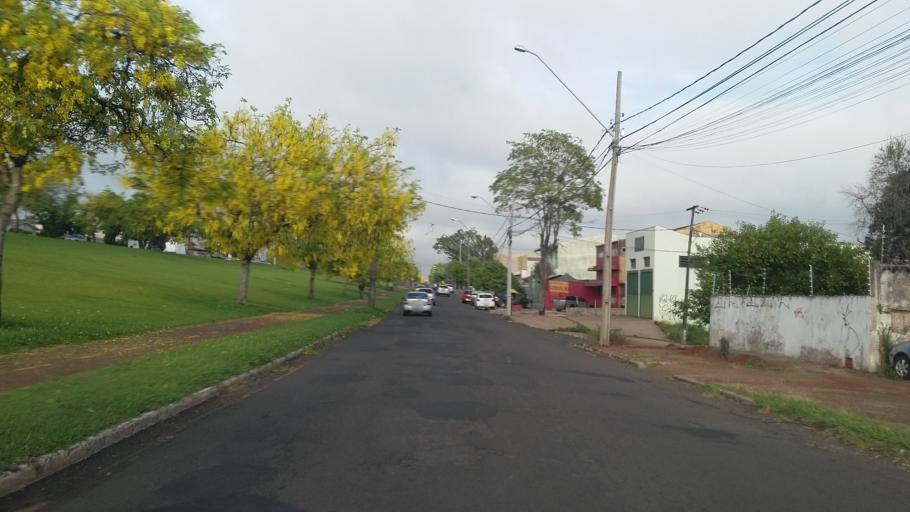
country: BR
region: Parana
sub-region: Londrina
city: Londrina
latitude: -23.2970
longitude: -51.1835
